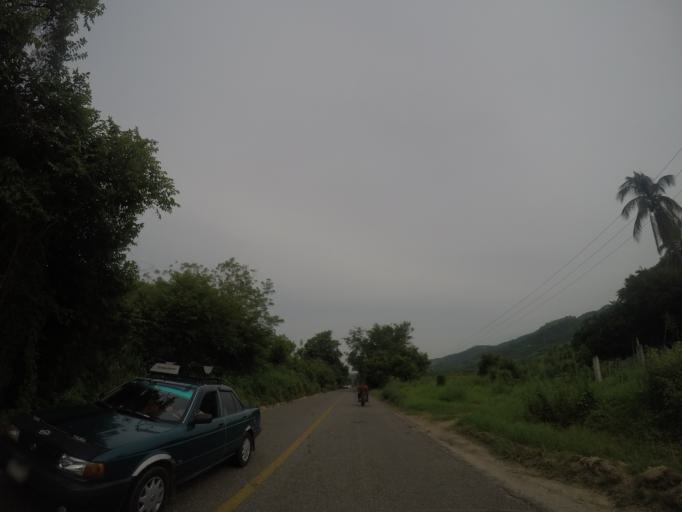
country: MX
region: Oaxaca
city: San Pedro Mixtepec
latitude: 15.9336
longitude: -97.1520
